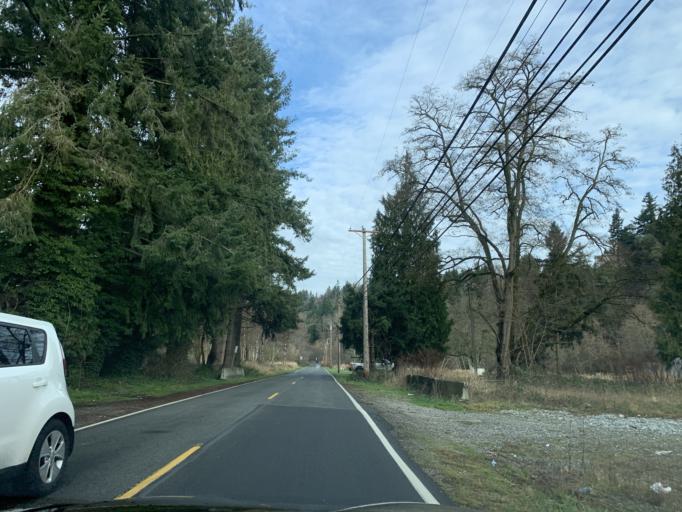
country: US
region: Washington
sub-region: Pierce County
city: Fife Heights
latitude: 47.2466
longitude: -122.3469
